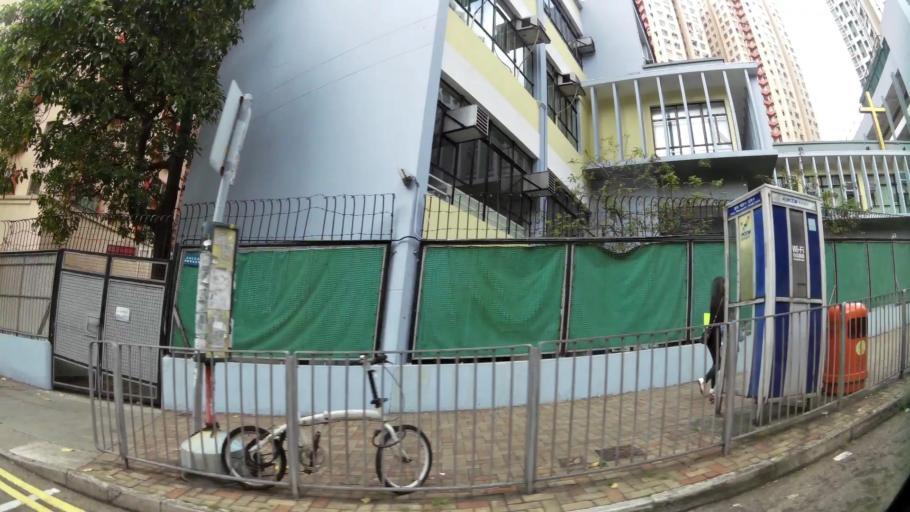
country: HK
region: Kowloon City
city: Kowloon
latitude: 22.3250
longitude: 114.2170
